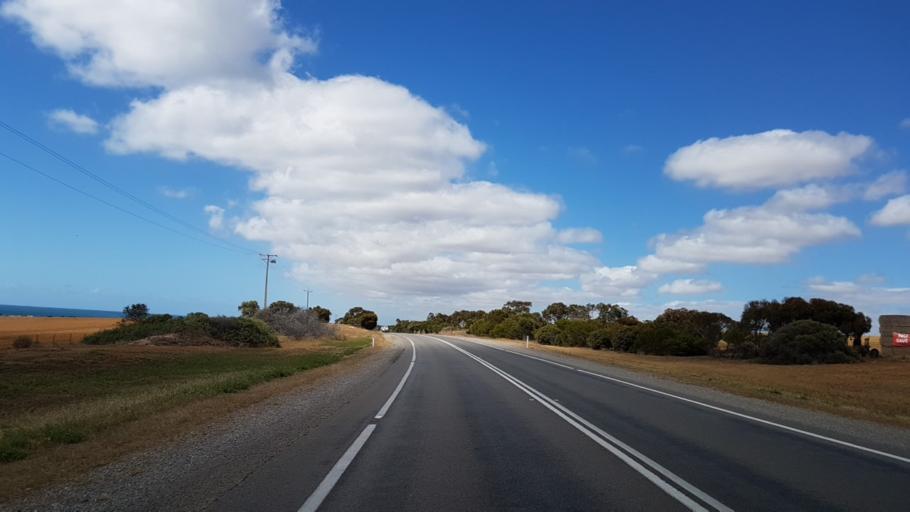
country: AU
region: South Australia
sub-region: Yorke Peninsula
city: Ardrossan
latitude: -34.4807
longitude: 137.8890
